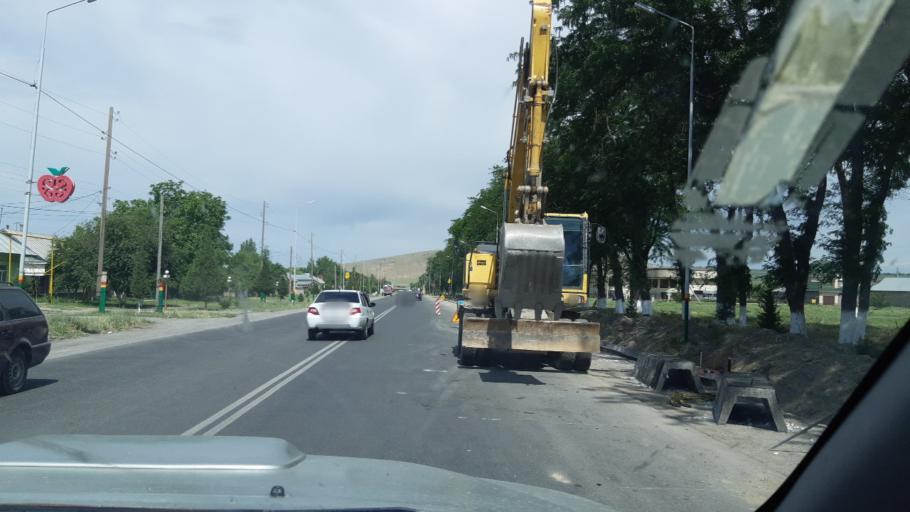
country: KZ
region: Ongtustik Qazaqstan
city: Turar Ryskulov
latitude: 42.5436
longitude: 70.3330
